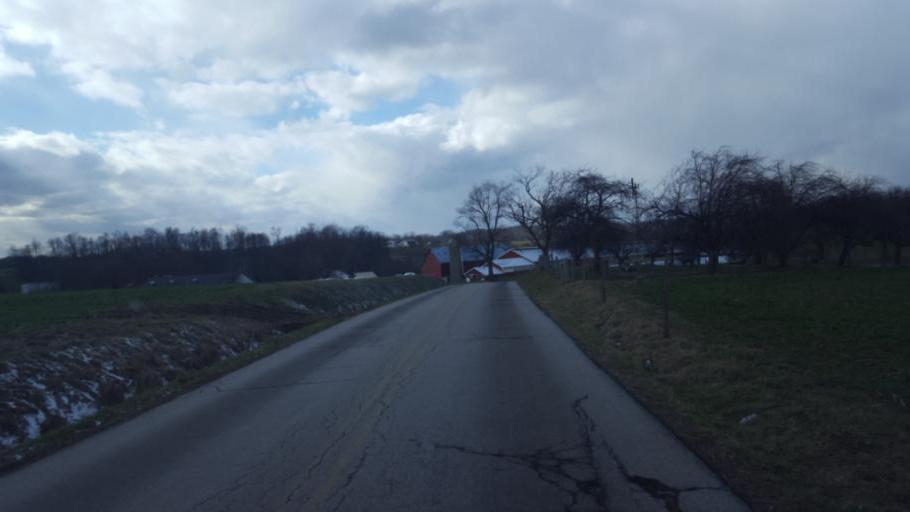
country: US
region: Ohio
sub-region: Tuscarawas County
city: Sugarcreek
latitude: 40.5026
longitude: -81.7313
